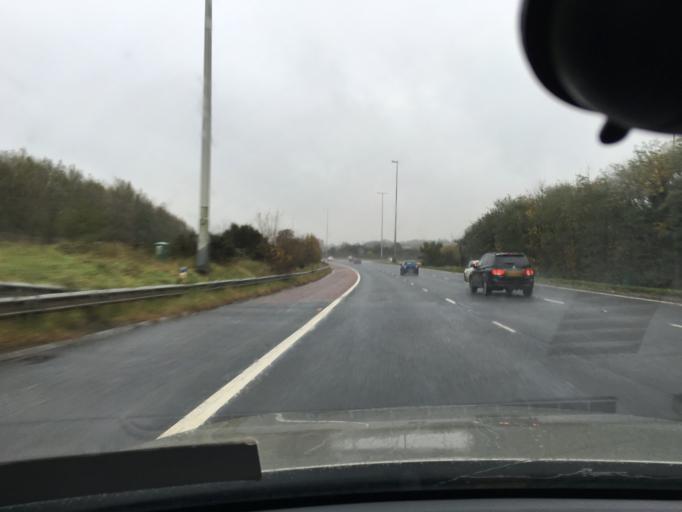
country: GB
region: Northern Ireland
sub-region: Newtownabbey District
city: Newtownabbey
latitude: 54.6419
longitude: -5.9166
